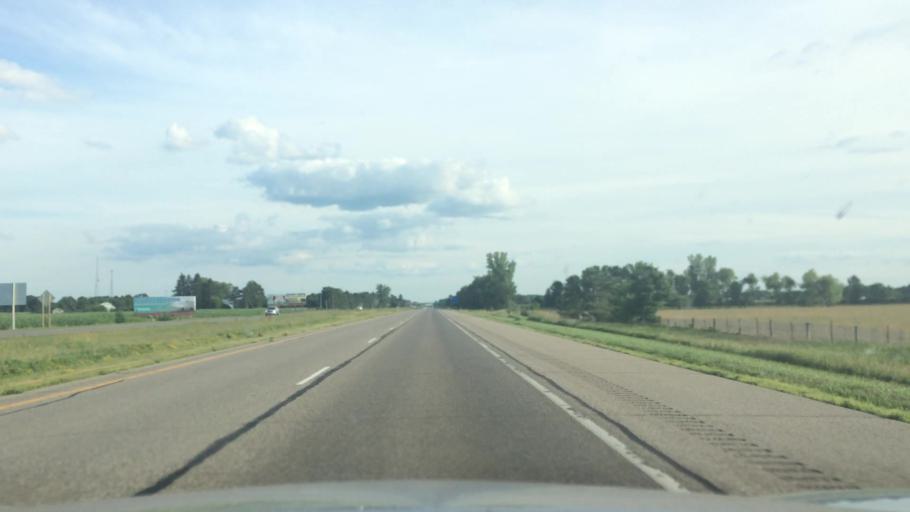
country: US
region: Wisconsin
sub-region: Portage County
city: Plover
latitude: 44.3231
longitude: -89.5235
